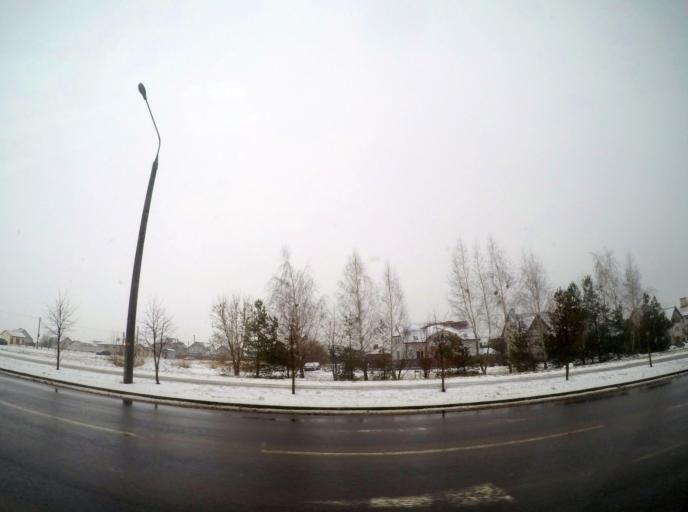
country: BY
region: Grodnenskaya
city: Hrodna
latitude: 53.6205
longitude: 23.8222
